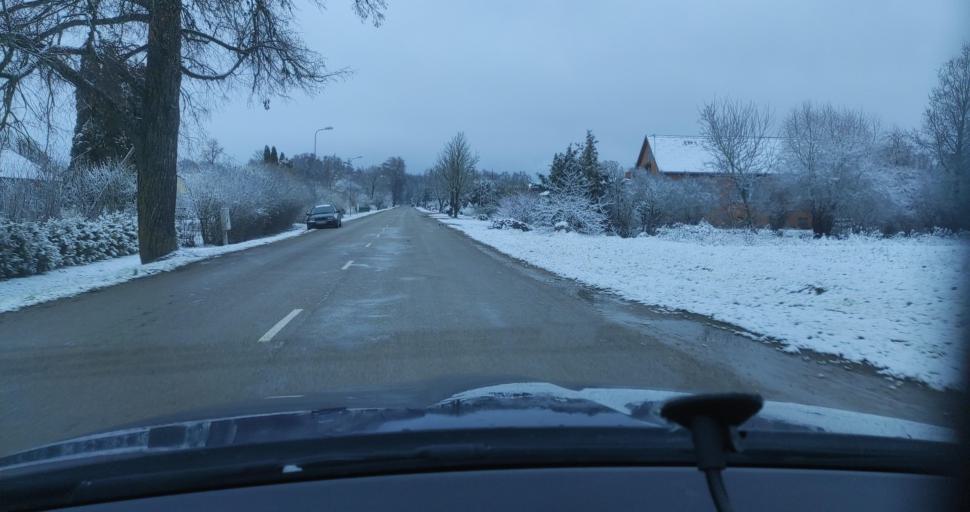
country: LV
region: Skrunda
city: Skrunda
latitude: 56.8685
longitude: 22.2335
